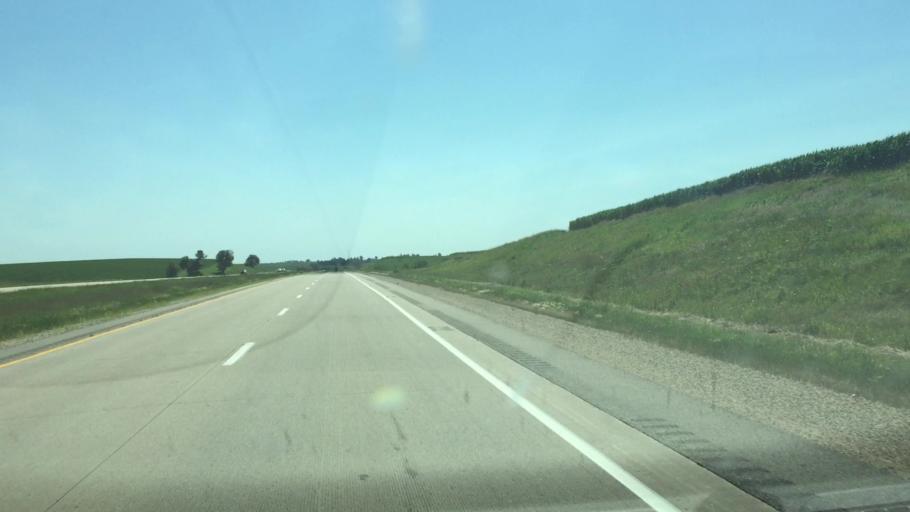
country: US
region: Iowa
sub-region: Dubuque County
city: Peosta
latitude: 42.3554
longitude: -90.8192
